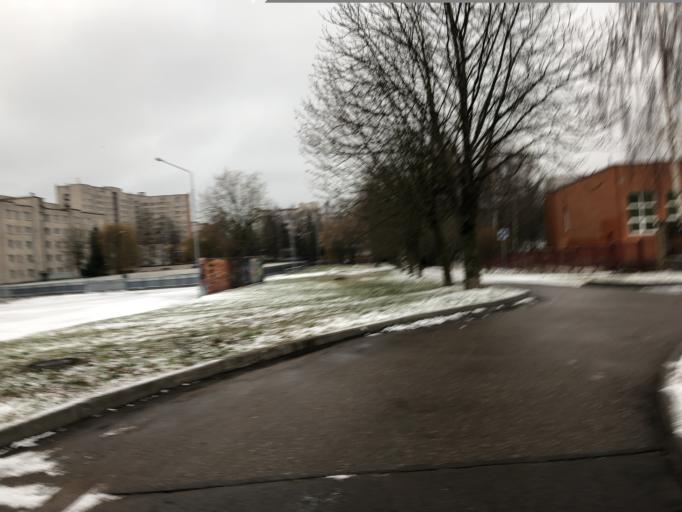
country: BY
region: Grodnenskaya
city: Hrodna
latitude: 53.7009
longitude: 23.8136
